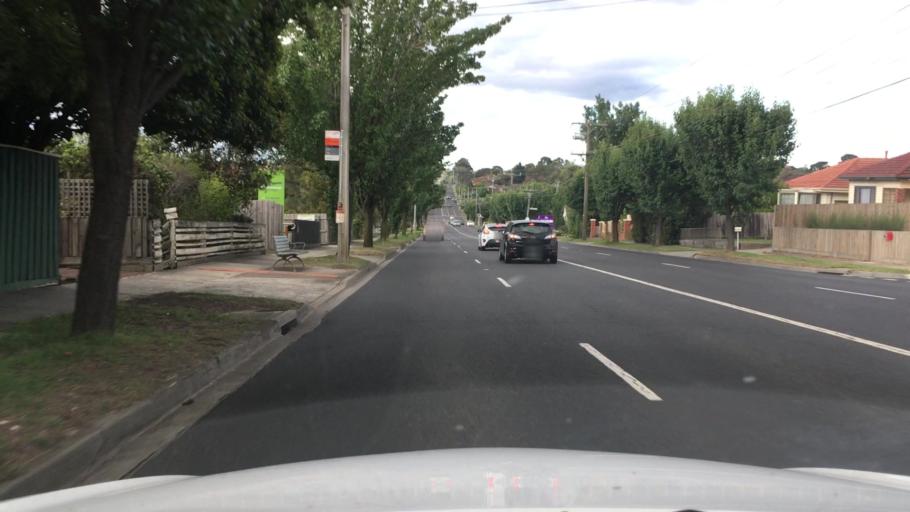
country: AU
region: Victoria
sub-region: Whitehorse
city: Burwood
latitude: -37.8434
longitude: 145.1339
